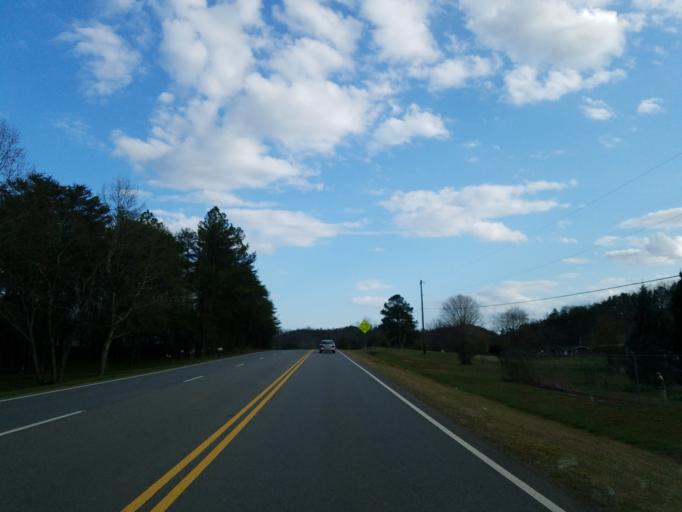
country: US
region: Georgia
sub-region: Bartow County
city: Rydal
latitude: 34.4420
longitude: -84.7226
